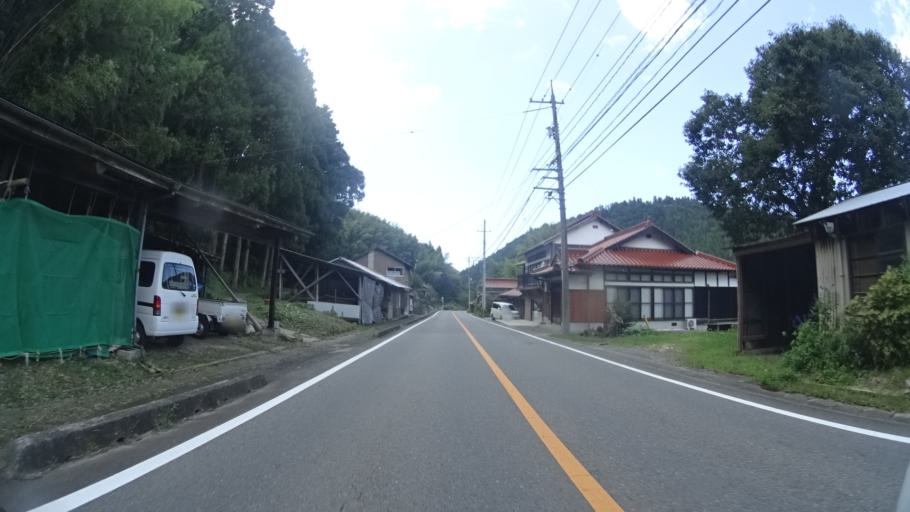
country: JP
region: Yamaguchi
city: Hagi
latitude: 34.4365
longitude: 131.4646
